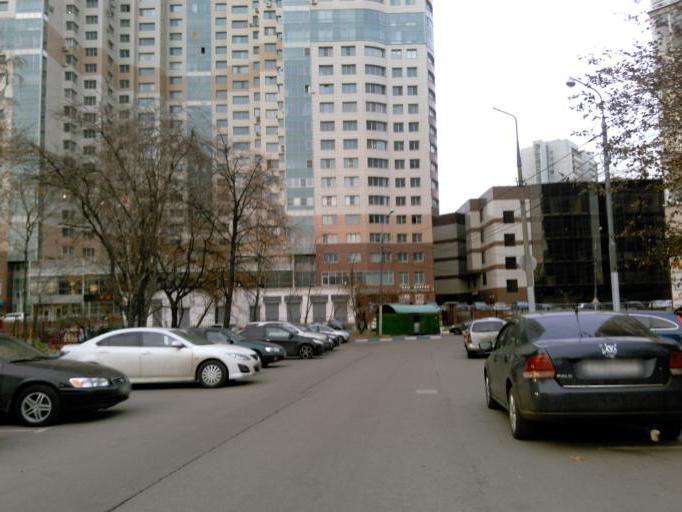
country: RU
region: Moscow
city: Troparevo
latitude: 55.6603
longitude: 37.5099
